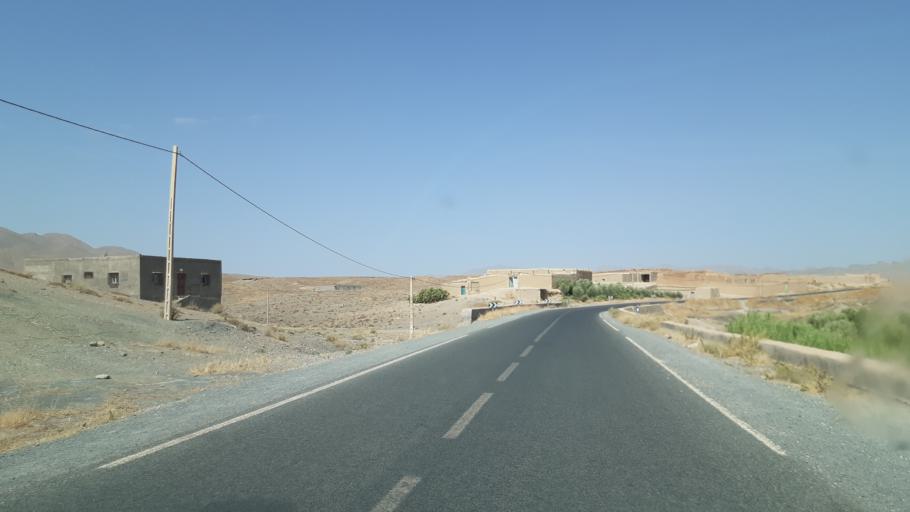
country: MA
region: Meknes-Tafilalet
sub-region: Errachidia
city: Amouguer
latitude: 32.2216
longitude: -4.6957
